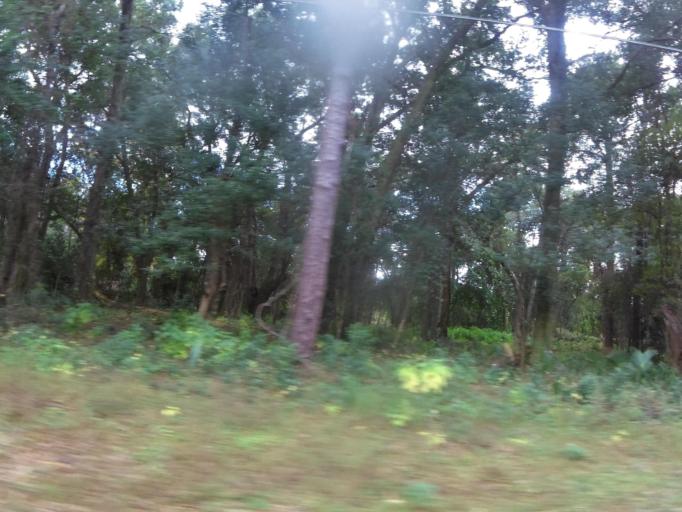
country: US
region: Florida
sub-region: Duval County
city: Jacksonville
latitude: 30.3236
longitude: -81.5901
